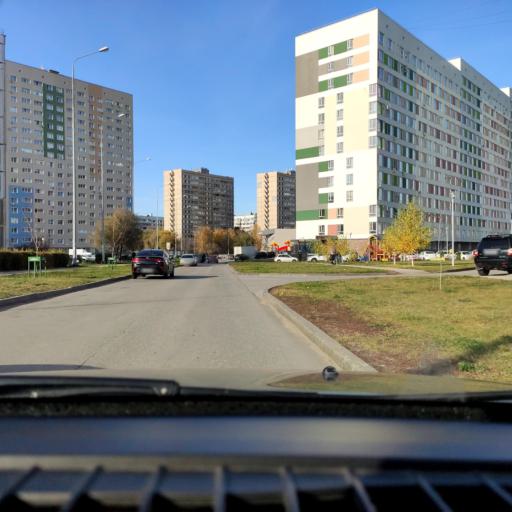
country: RU
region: Samara
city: Tol'yatti
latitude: 53.5284
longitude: 49.3411
